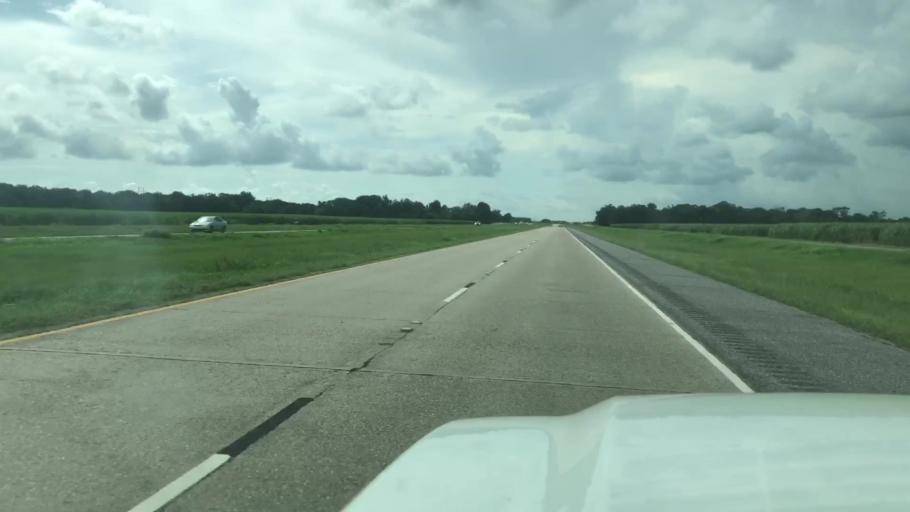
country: US
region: Louisiana
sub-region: Saint Mary Parish
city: Franklin
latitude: 29.7618
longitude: -91.4807
